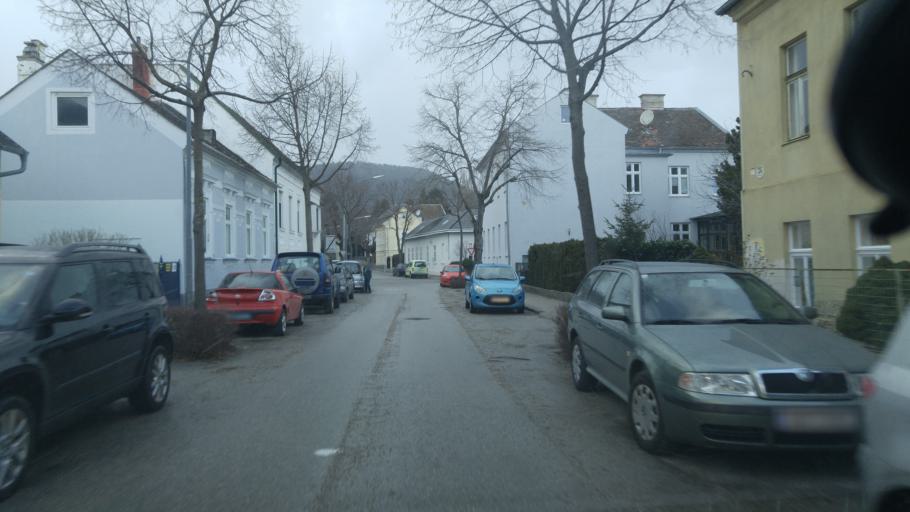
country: AT
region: Lower Austria
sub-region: Politischer Bezirk Baden
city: Baden
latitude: 47.9997
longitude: 16.2157
